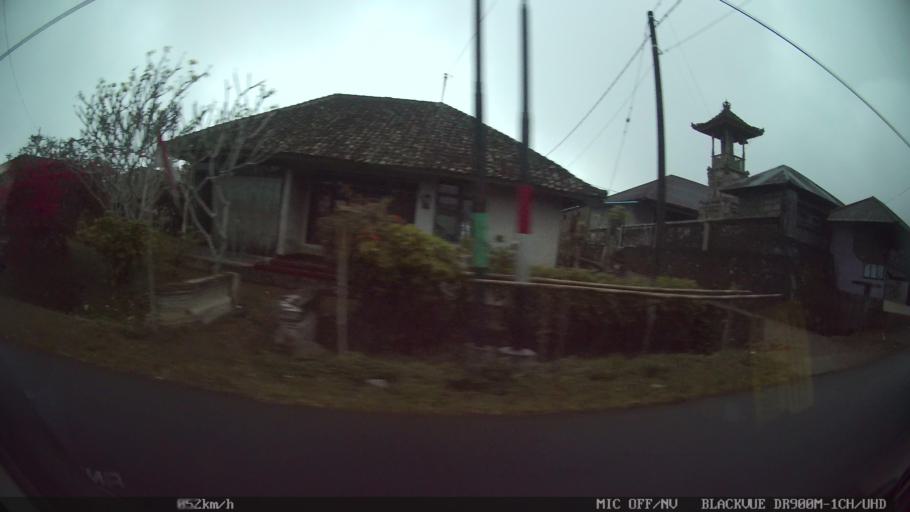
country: ID
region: Bali
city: Klau
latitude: -8.3570
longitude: 115.0288
